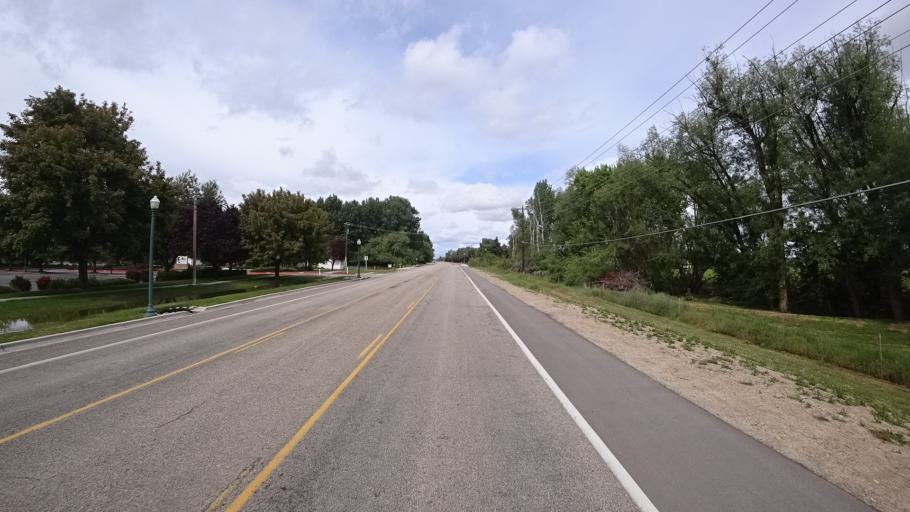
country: US
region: Idaho
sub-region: Ada County
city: Eagle
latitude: 43.6956
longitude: -116.3672
